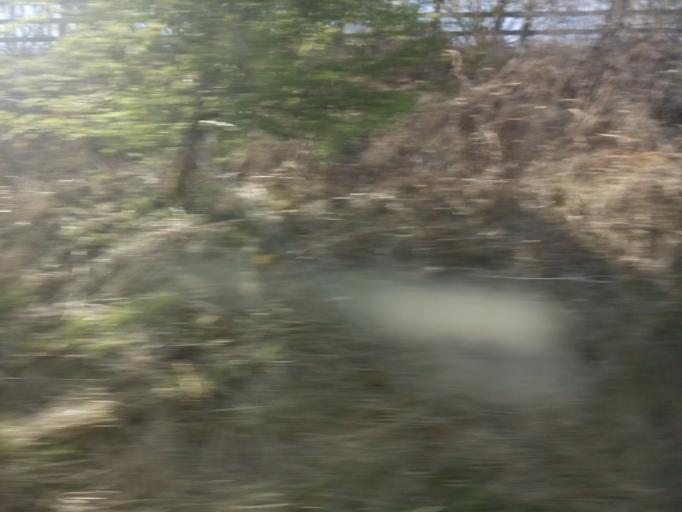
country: GB
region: Scotland
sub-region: East Lothian
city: East Linton
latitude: 55.9885
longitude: -2.5922
